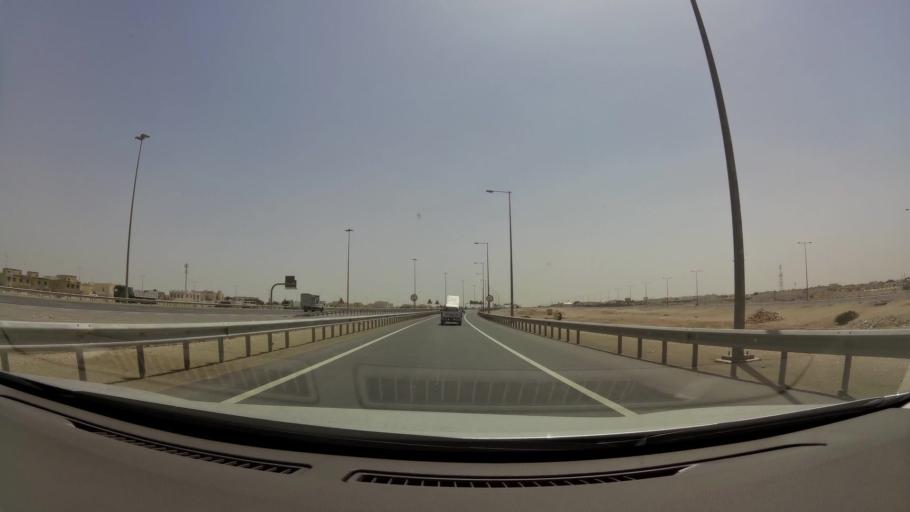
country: QA
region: Baladiyat Umm Salal
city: Umm Salal `Ali
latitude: 25.4795
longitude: 51.4068
